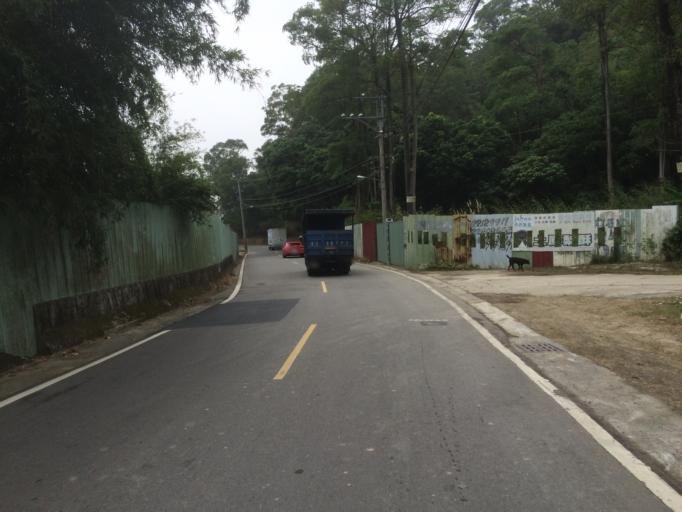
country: TW
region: Taiwan
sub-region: Taichung City
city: Taichung
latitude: 24.1615
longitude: 120.7440
